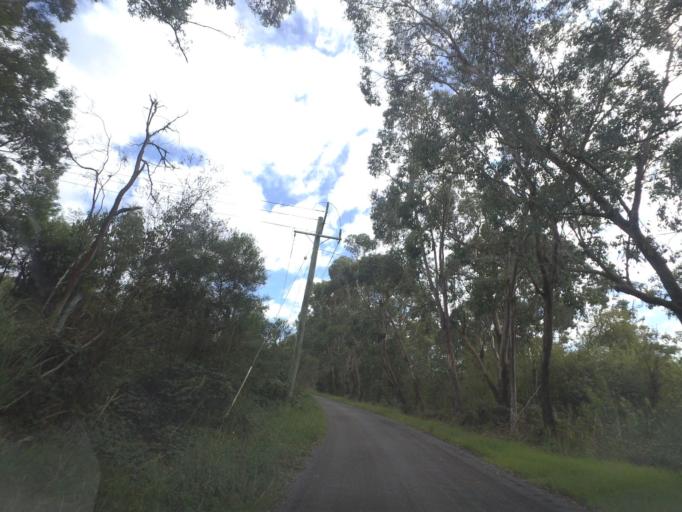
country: AU
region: Victoria
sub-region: Yarra Ranges
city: Mount Evelyn
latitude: -37.7891
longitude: 145.4106
